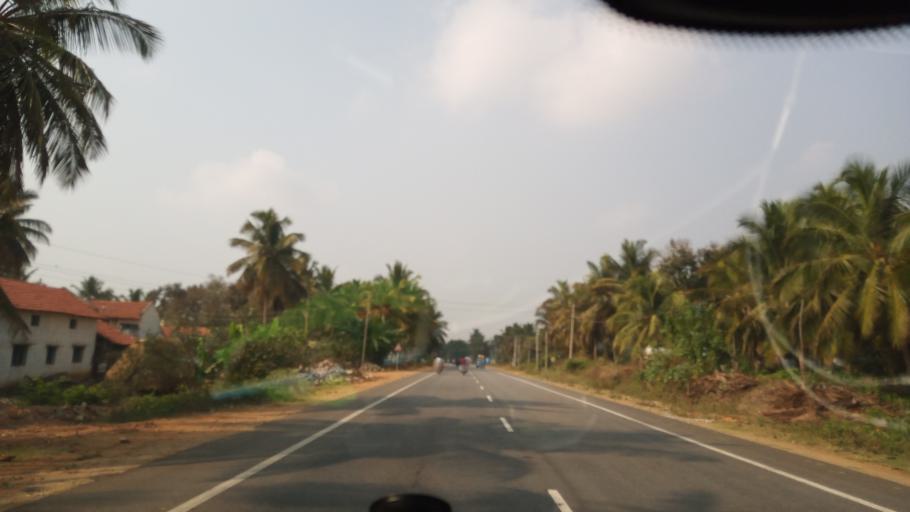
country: IN
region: Karnataka
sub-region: Mandya
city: Nagamangala
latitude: 12.7712
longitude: 76.7400
